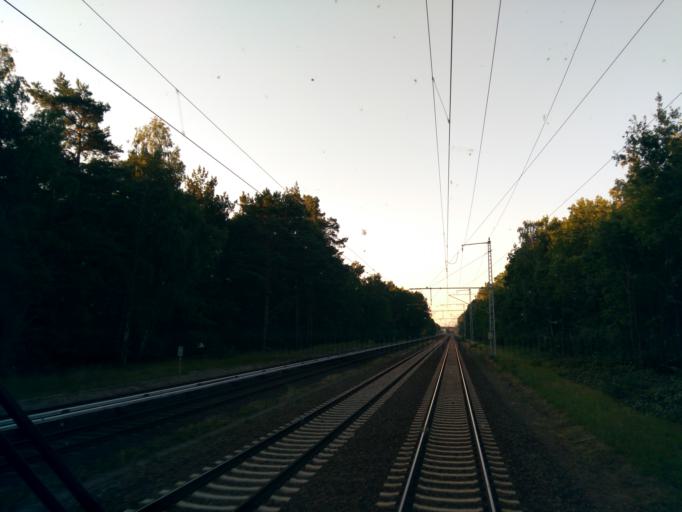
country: DE
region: Brandenburg
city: Zeuthen
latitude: 52.3818
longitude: 13.6084
